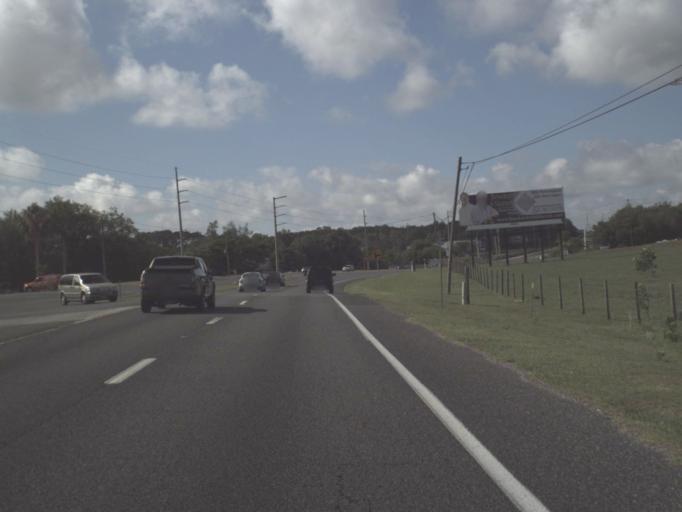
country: US
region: Florida
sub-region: Lake County
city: Fruitland Park
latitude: 28.8910
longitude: -81.9071
